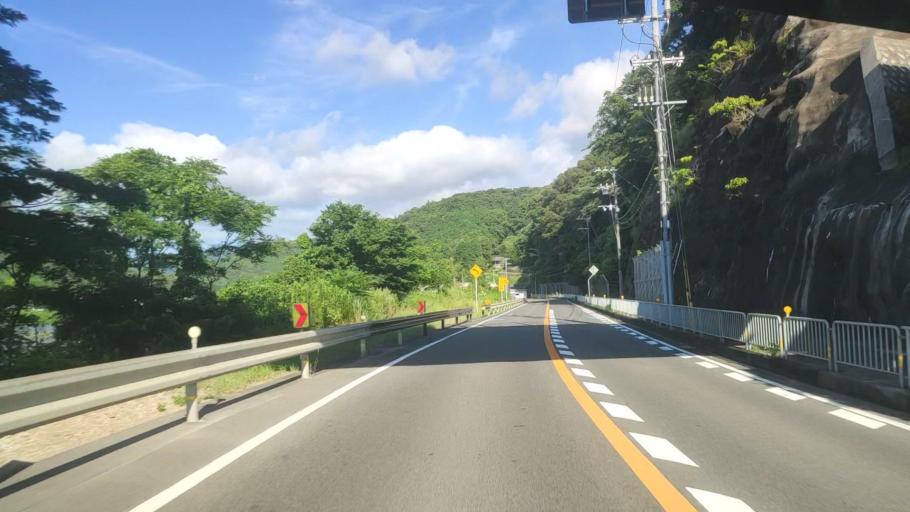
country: JP
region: Wakayama
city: Tanabe
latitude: 33.6635
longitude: 135.4026
